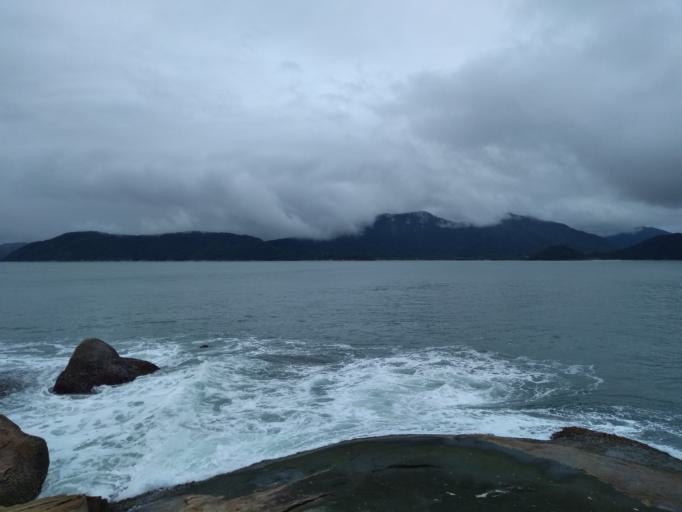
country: BR
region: Sao Paulo
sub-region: Ubatuba
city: Ubatuba
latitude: -23.5296
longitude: -45.1578
